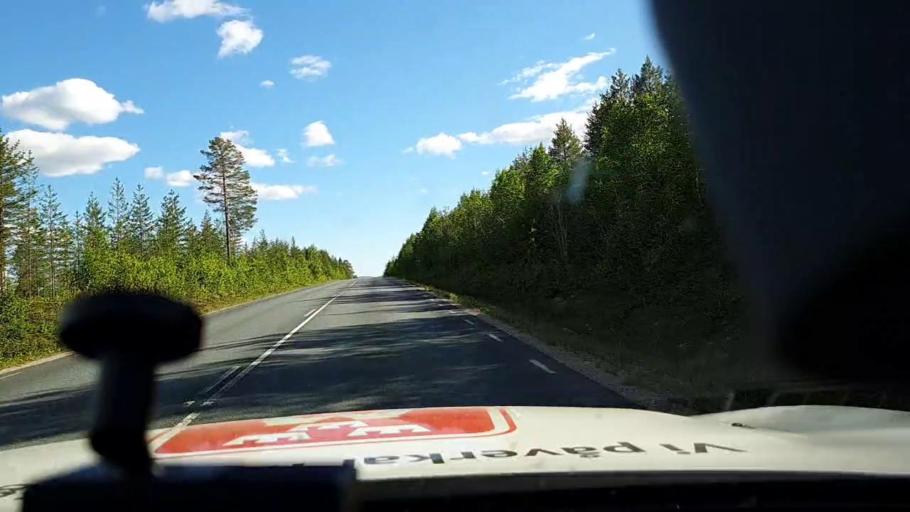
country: SE
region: Norrbotten
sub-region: Overtornea Kommun
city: OEvertornea
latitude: 66.3517
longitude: 23.6478
